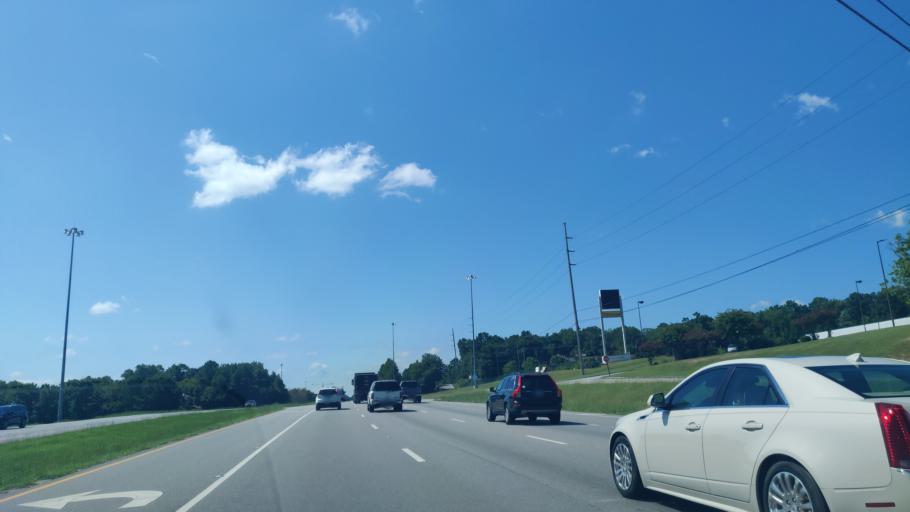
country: US
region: Alabama
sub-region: Russell County
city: Phenix City
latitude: 32.4820
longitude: -85.0309
